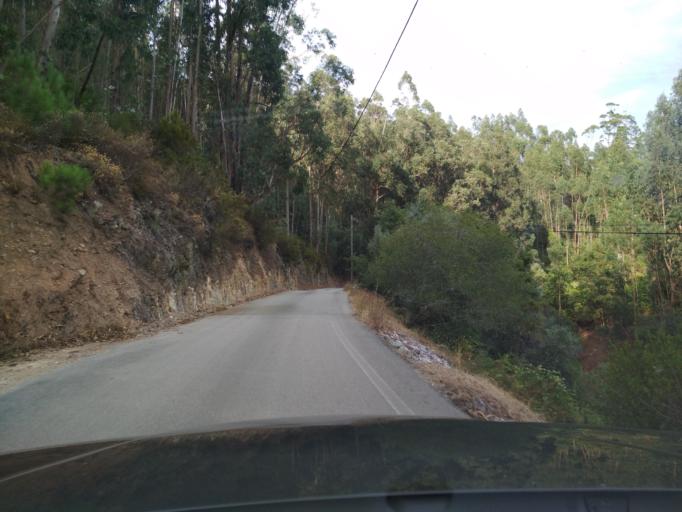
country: PT
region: Coimbra
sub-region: Coimbra
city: Coimbra
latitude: 40.2503
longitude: -8.3877
